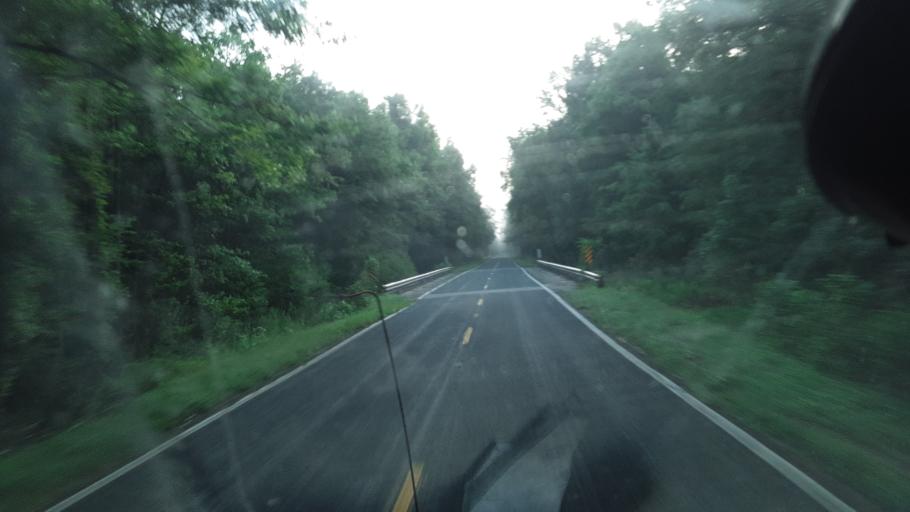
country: US
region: South Carolina
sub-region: Clarendon County
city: Manning
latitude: 33.7547
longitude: -80.0638
